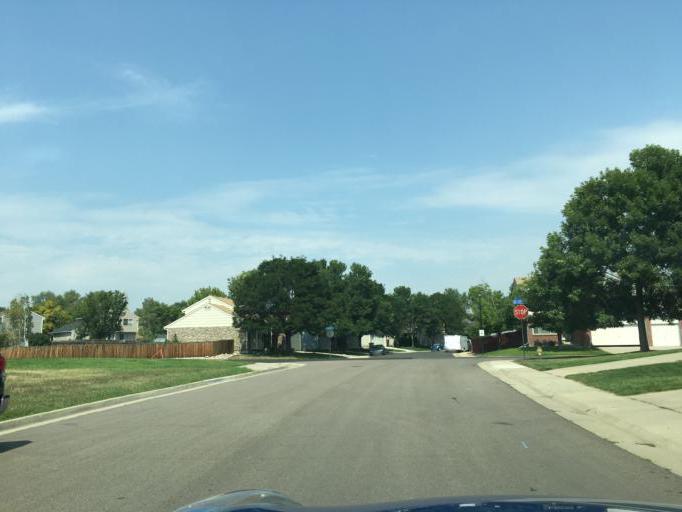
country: US
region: Colorado
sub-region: Adams County
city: Northglenn
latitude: 39.9228
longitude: -105.0209
